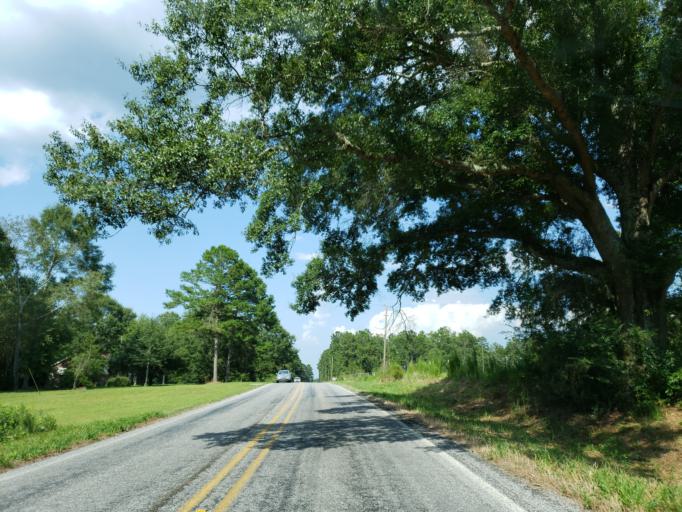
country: US
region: Mississippi
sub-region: Covington County
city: Collins
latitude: 31.6204
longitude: -89.3768
